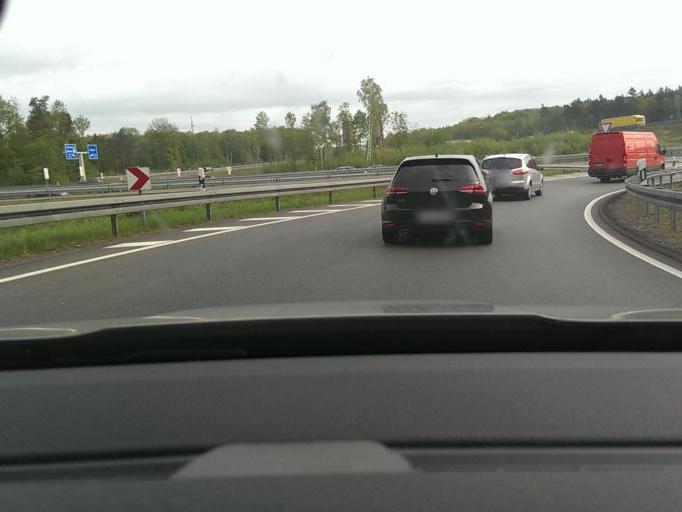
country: DE
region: Lower Saxony
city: Lehrte
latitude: 52.3964
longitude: 9.8974
